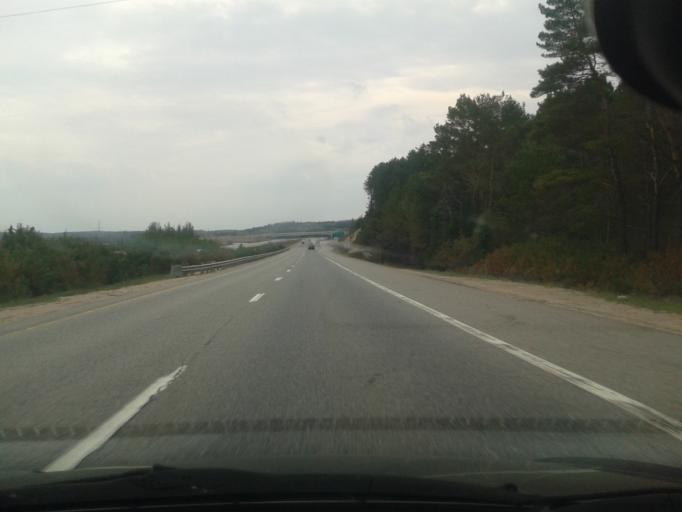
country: CA
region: Ontario
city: Powassan
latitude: 46.0045
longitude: -79.3590
